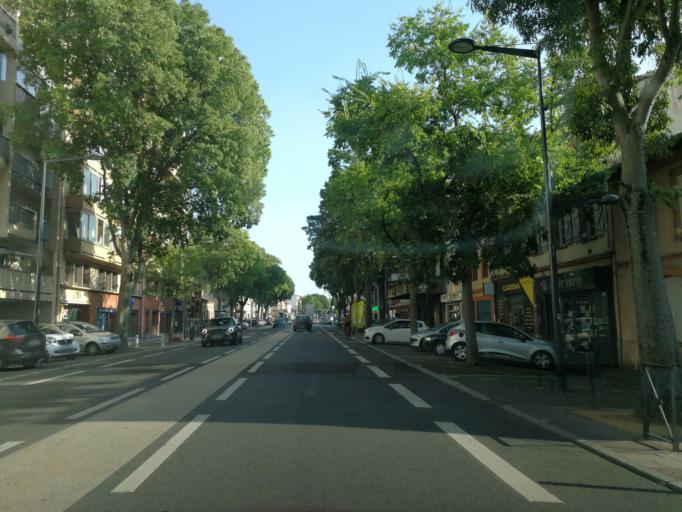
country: FR
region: Midi-Pyrenees
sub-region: Departement de la Haute-Garonne
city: Toulouse
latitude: 43.6219
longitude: 1.4351
